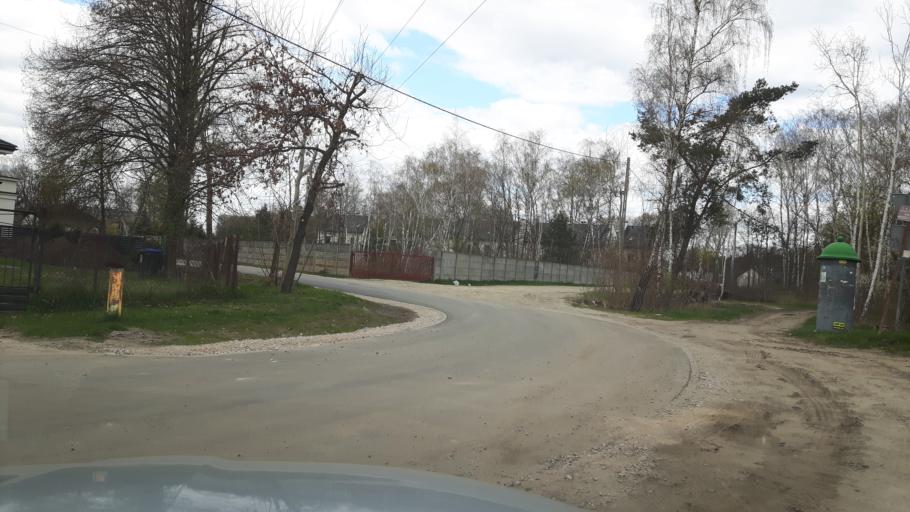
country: PL
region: Masovian Voivodeship
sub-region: Powiat wolominski
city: Kobylka
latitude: 52.3512
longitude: 21.2150
